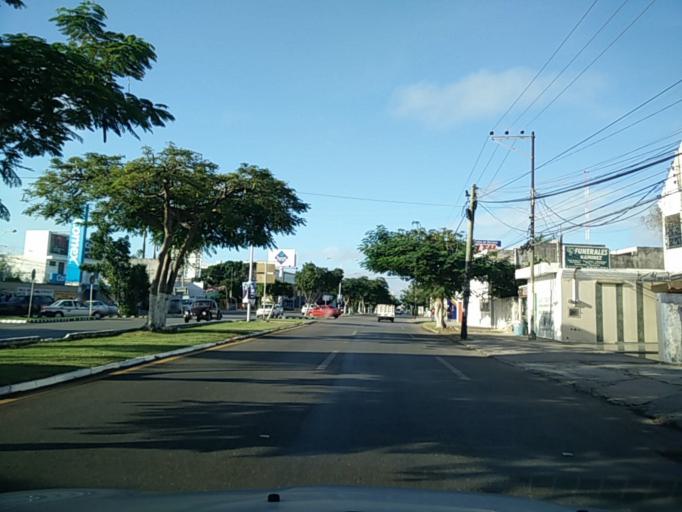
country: MX
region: Yucatan
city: Merida
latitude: 20.9506
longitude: -89.6474
